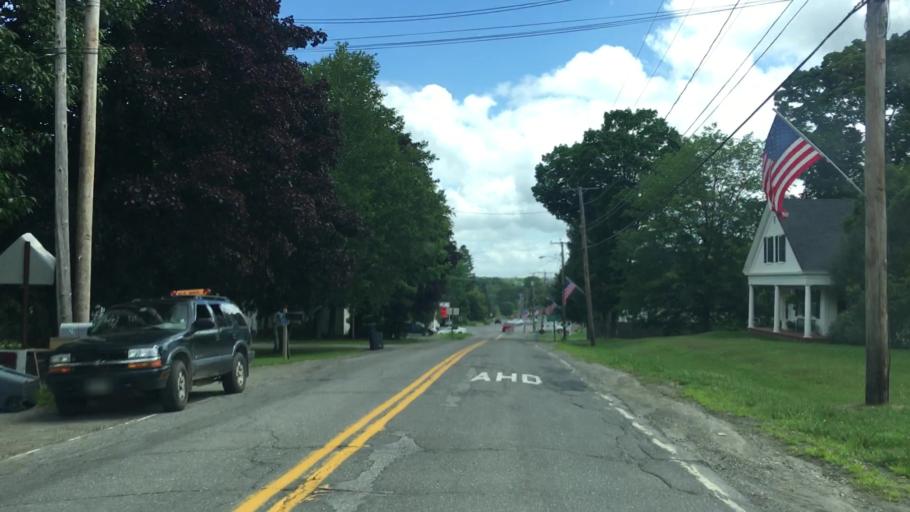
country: US
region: Maine
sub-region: Penobscot County
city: Carmel
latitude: 44.7966
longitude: -69.0537
